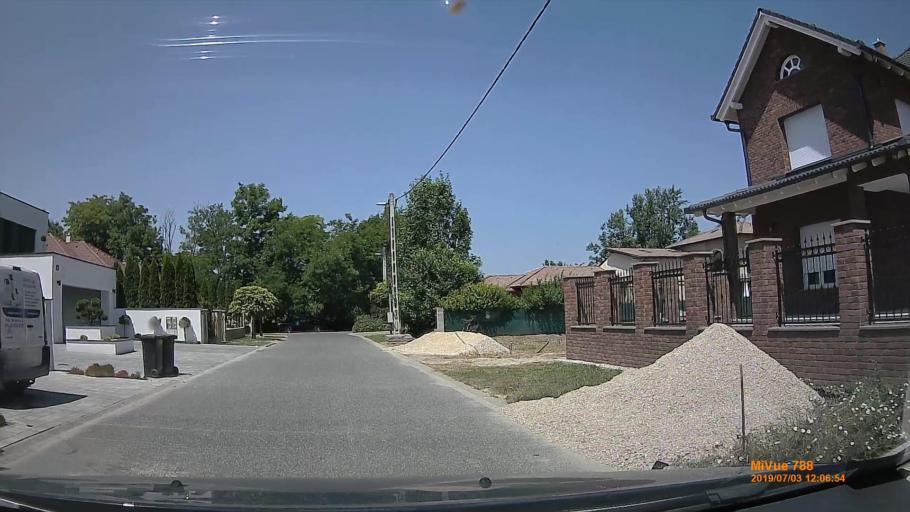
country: HU
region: Gyor-Moson-Sopron
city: Gyor
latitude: 47.7186
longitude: 17.6118
